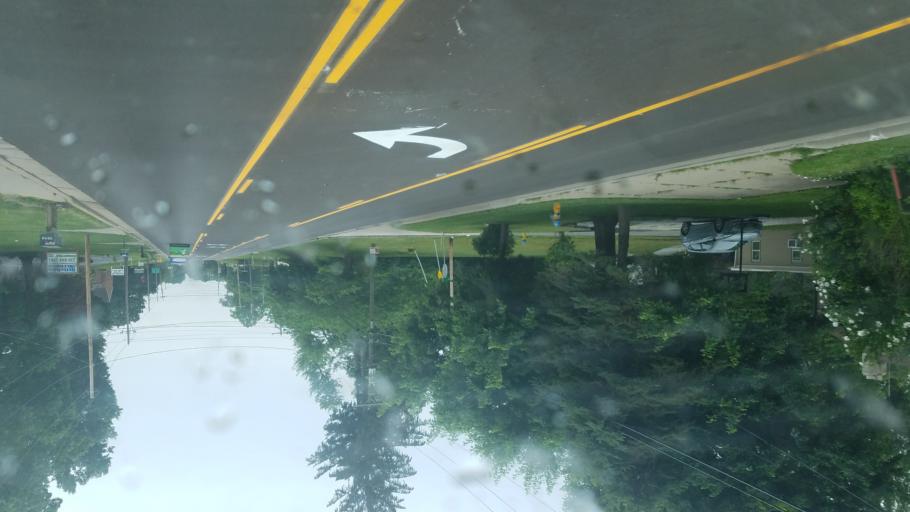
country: US
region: Ohio
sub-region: Summit County
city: Portage Lakes
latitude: 41.0019
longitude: -81.5566
